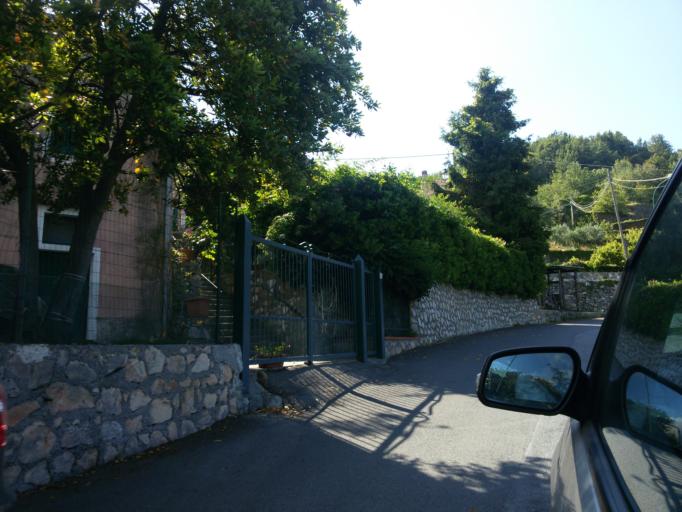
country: IT
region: Liguria
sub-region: Provincia di Savona
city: Borgio
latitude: 44.1781
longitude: 8.3036
